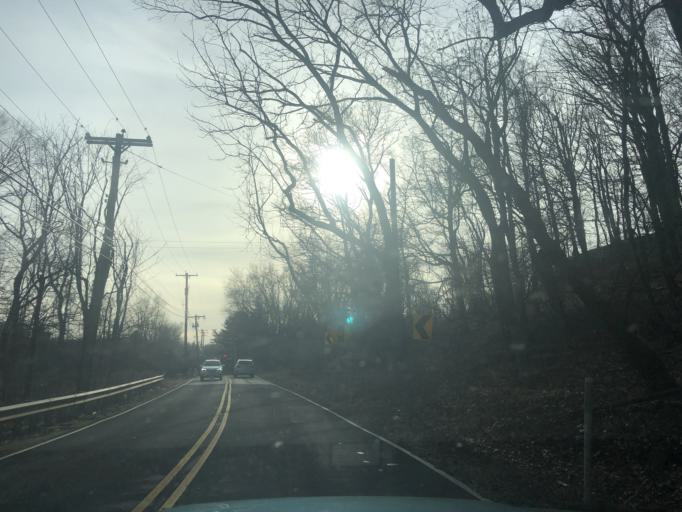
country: US
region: Pennsylvania
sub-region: Montgomery County
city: Plymouth Meeting
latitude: 40.1191
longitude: -75.2476
